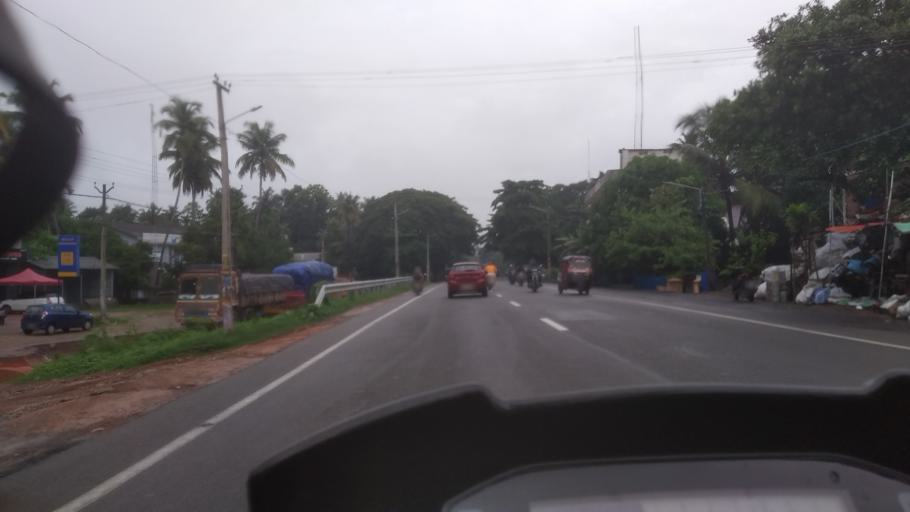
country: IN
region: Kerala
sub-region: Alappuzha
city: Kayankulam
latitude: 9.1863
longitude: 76.4891
